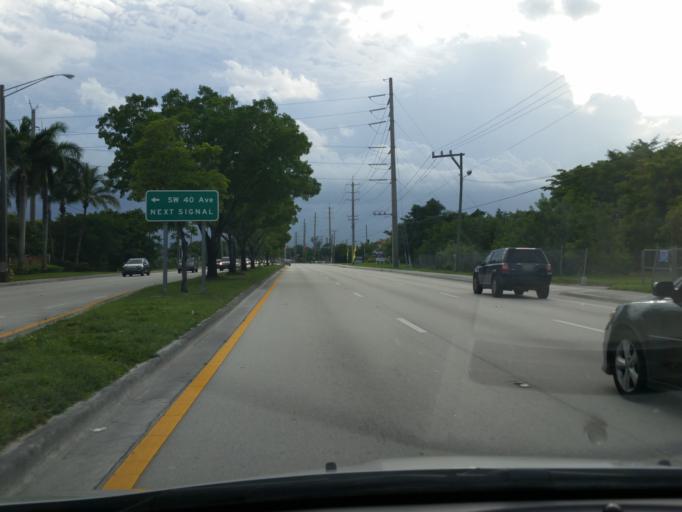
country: US
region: Florida
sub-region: Broward County
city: Davie
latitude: 26.0628
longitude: -80.1972
